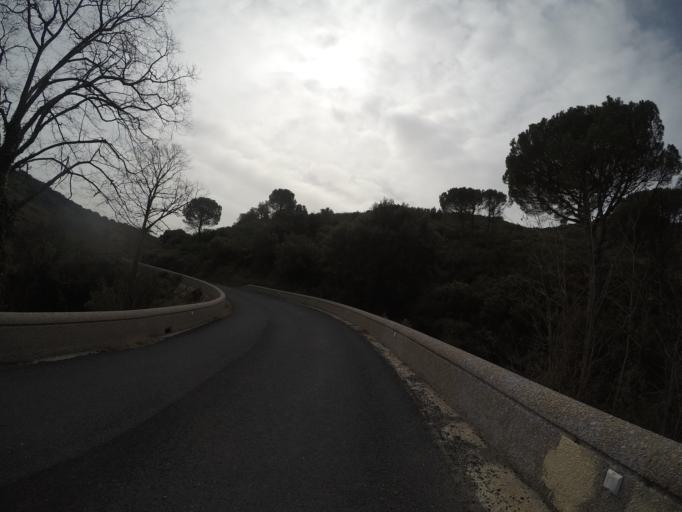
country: FR
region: Languedoc-Roussillon
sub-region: Departement des Pyrenees-Orientales
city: Estagel
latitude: 42.7435
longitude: 2.7254
